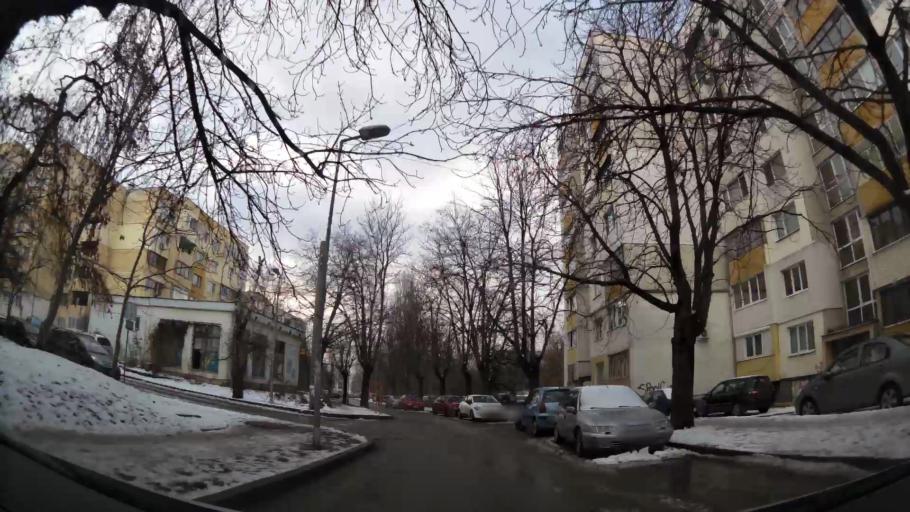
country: BG
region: Sofia-Capital
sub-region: Stolichna Obshtina
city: Sofia
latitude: 42.7081
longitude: 23.2934
